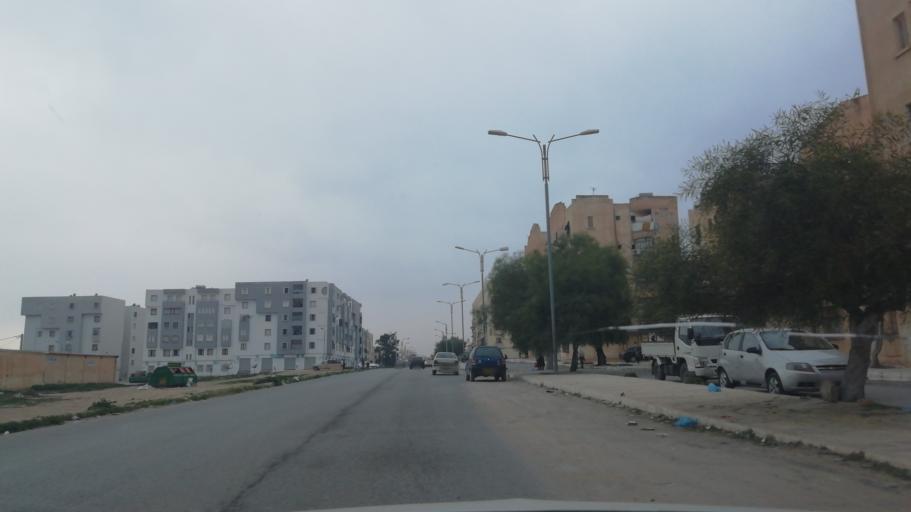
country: DZ
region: Sidi Bel Abbes
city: Sfizef
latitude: 35.2410
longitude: -0.2283
